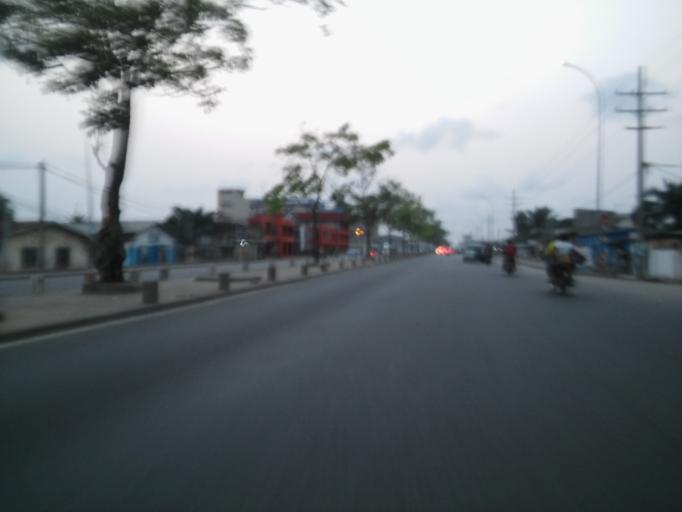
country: BJ
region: Littoral
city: Cotonou
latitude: 6.3766
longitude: 2.4010
